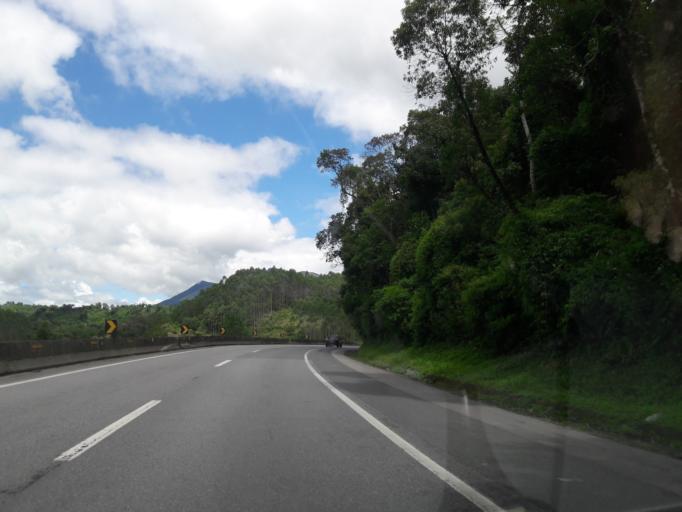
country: BR
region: Parana
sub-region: Antonina
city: Antonina
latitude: -25.1109
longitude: -48.7500
